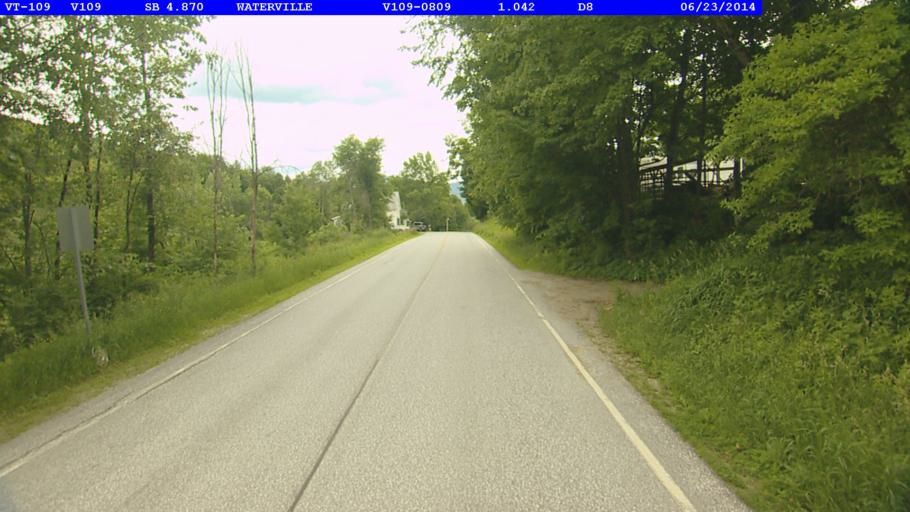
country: US
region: Vermont
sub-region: Lamoille County
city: Johnson
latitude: 44.6965
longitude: -72.7654
